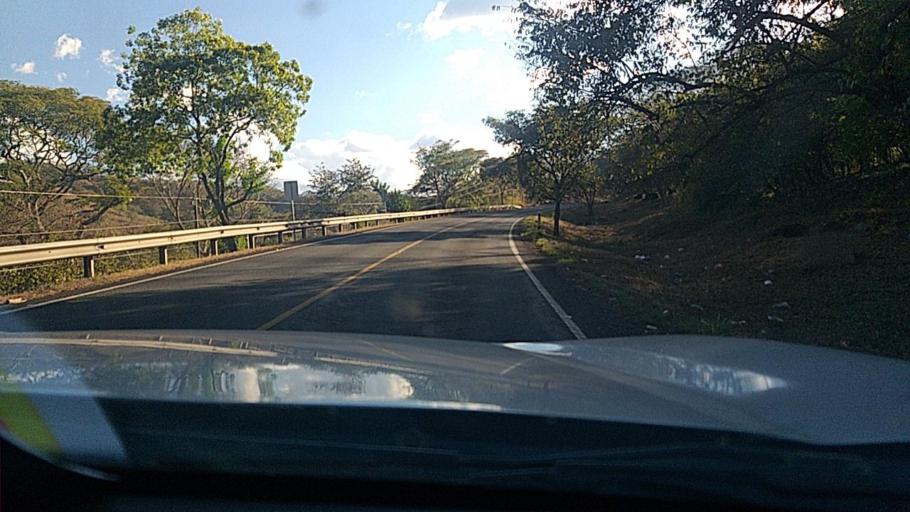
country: NI
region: Esteli
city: Condega
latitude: 13.2822
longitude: -86.3456
